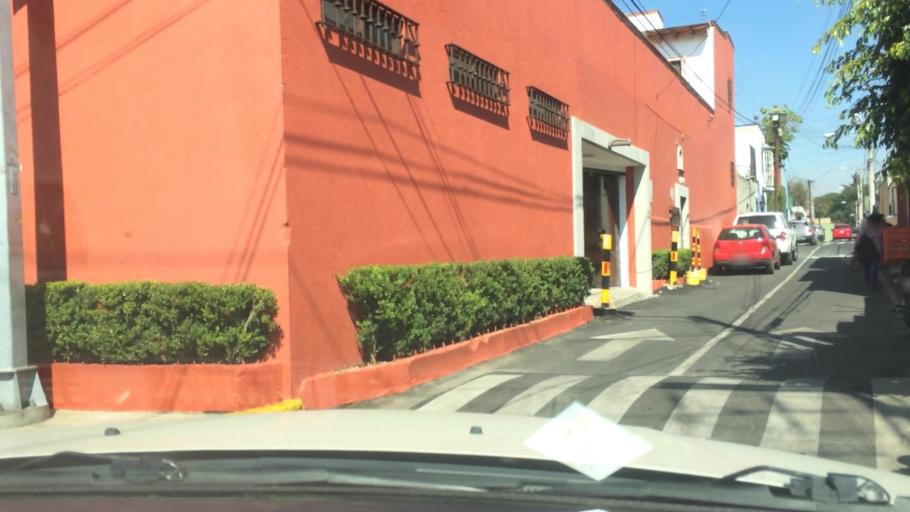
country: MX
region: Mexico City
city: Tlalpan
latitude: 19.2816
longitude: -99.1703
